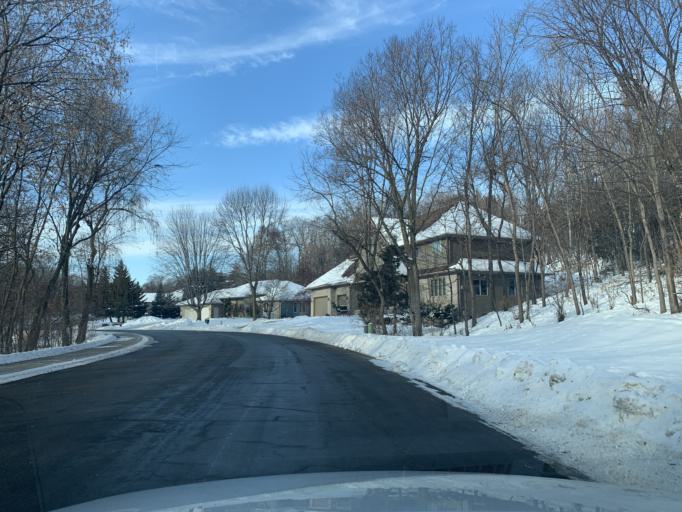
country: US
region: Minnesota
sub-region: Wright County
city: Saint Michael
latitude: 45.2043
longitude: -93.6571
